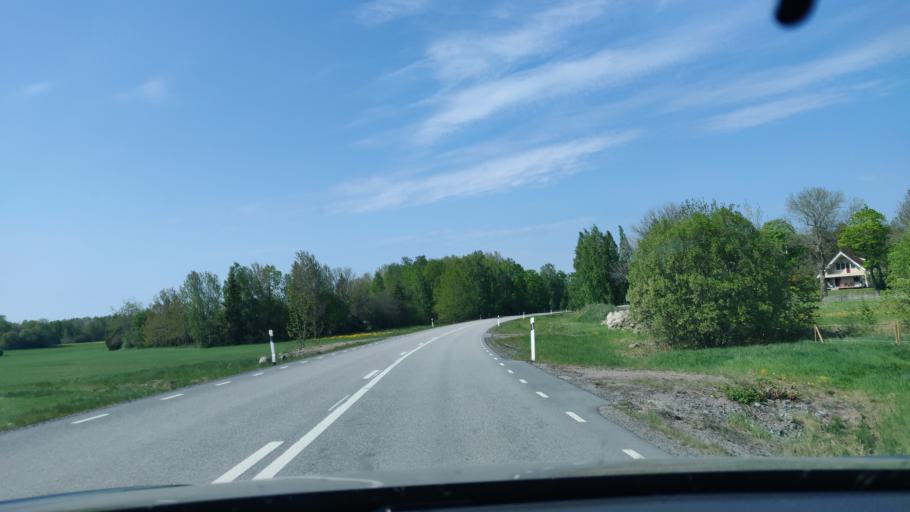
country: SE
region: Uppsala
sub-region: Heby Kommun
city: OEstervala
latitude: 60.1467
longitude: 17.2010
